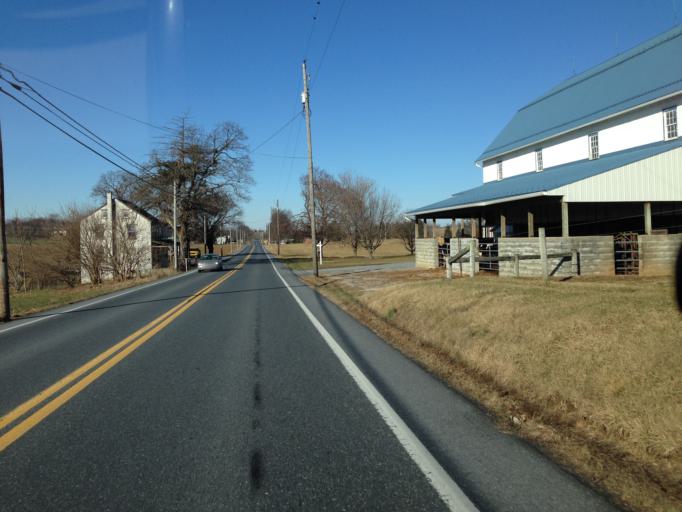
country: US
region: Pennsylvania
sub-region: Lancaster County
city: Penryn
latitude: 40.1766
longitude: -76.3434
